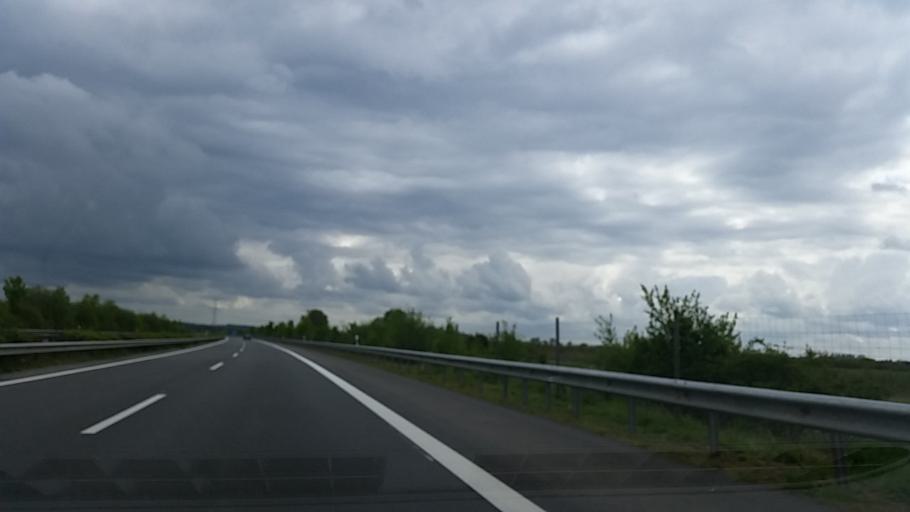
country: DE
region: Lower Saxony
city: Horneburg
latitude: 53.5280
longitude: 9.5800
